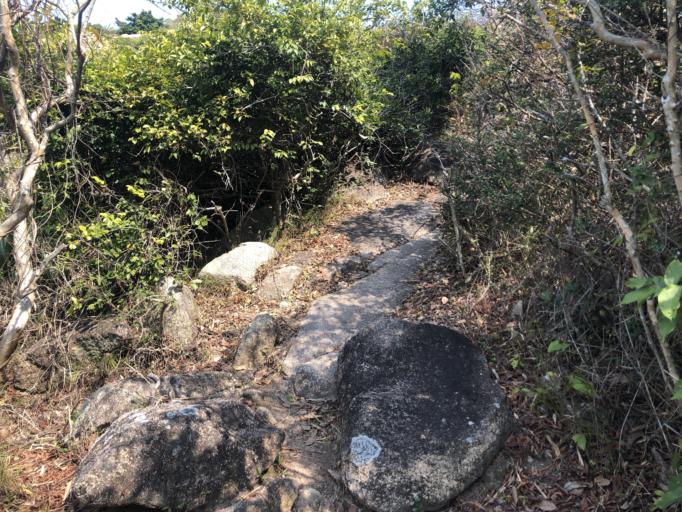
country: HK
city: Sok Kwu Wan
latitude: 22.1650
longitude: 114.2512
